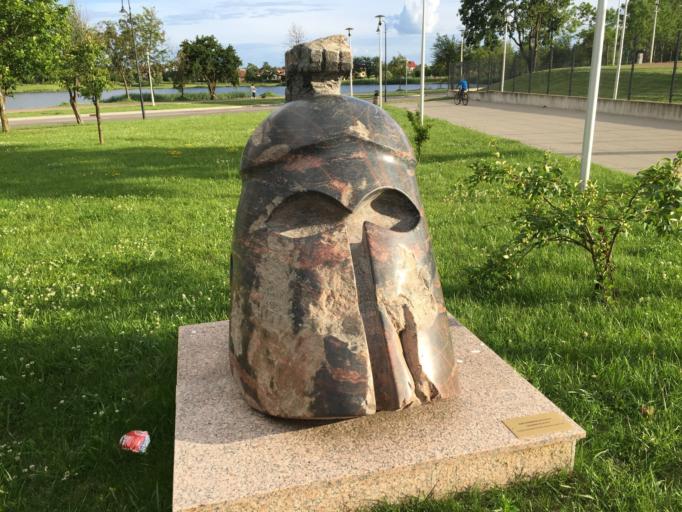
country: PL
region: Podlasie
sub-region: Suwalki
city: Suwalki
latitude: 54.0941
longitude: 22.9188
